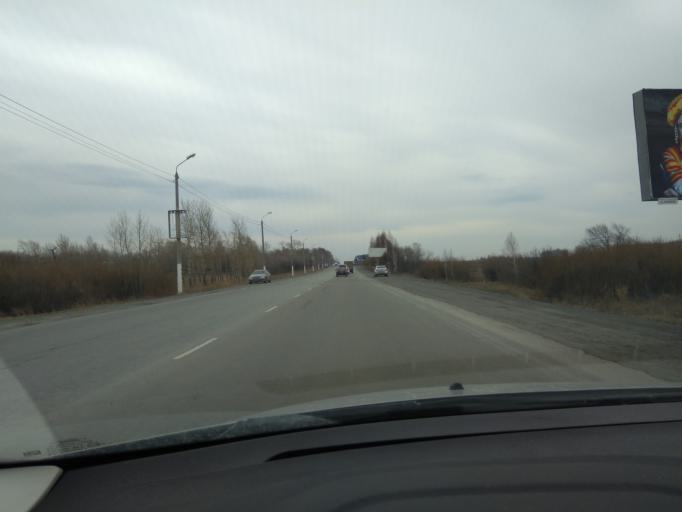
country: RU
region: Chelyabinsk
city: Potanino
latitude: 55.2938
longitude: 61.5114
